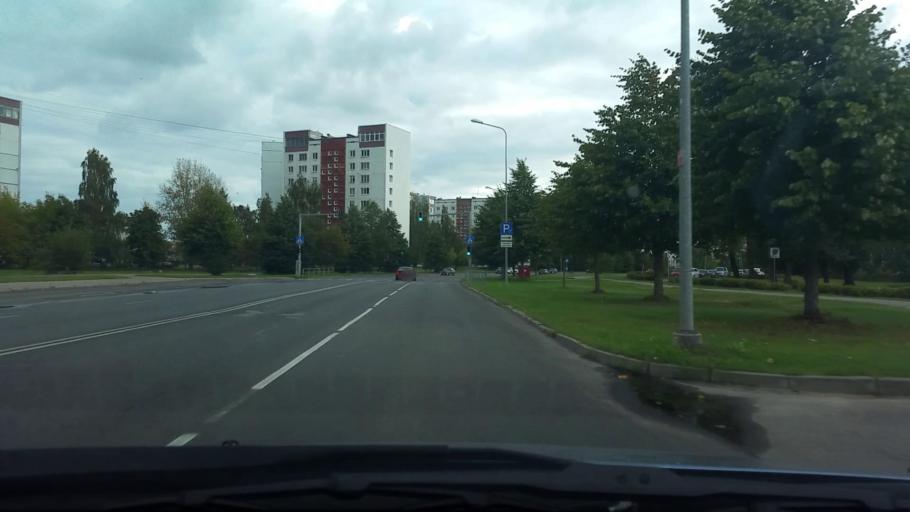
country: LV
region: Stopini
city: Ulbroka
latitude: 56.9662
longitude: 24.2332
